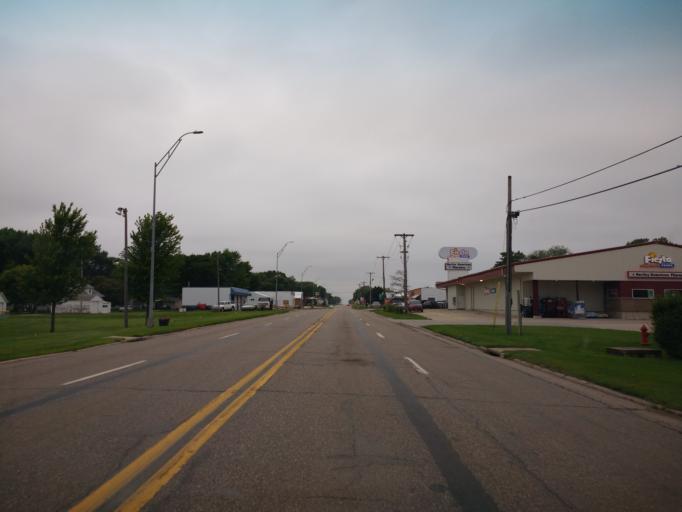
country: US
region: Iowa
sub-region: O'Brien County
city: Hartley
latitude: 43.1849
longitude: -95.4738
